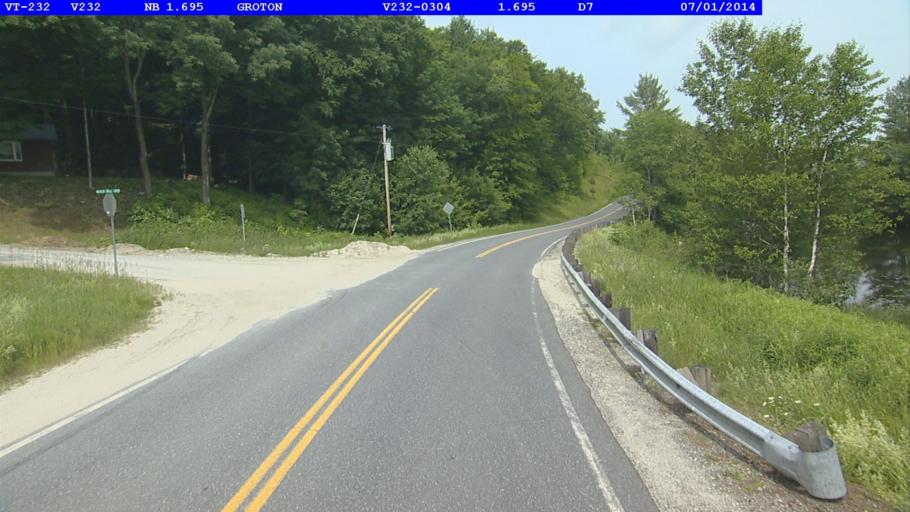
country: US
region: New Hampshire
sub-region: Grafton County
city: Woodsville
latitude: 44.2408
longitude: -72.2398
